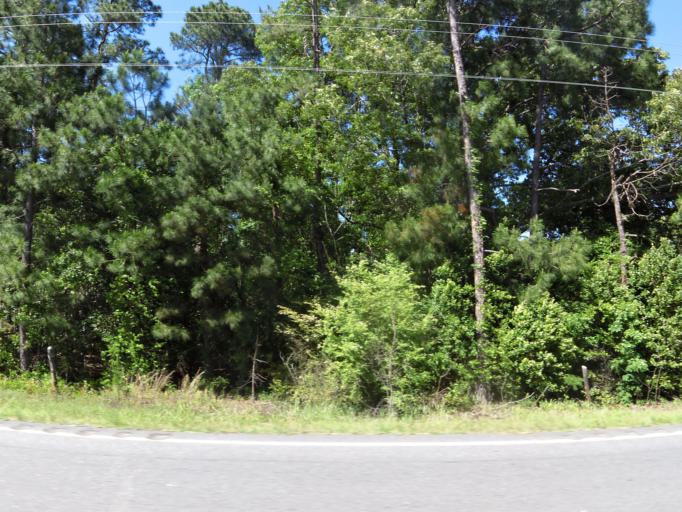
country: US
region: South Carolina
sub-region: Aiken County
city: Aiken
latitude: 33.5212
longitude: -81.6071
